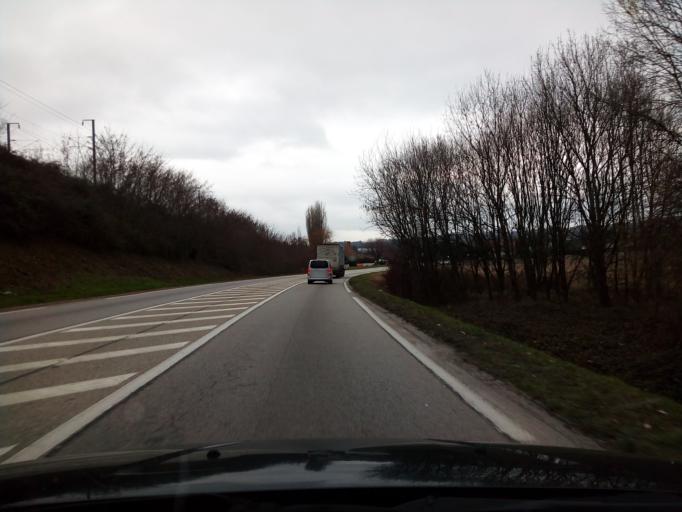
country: FR
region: Rhone-Alpes
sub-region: Departement de l'Isere
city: Moirans
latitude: 45.3275
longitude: 5.5723
